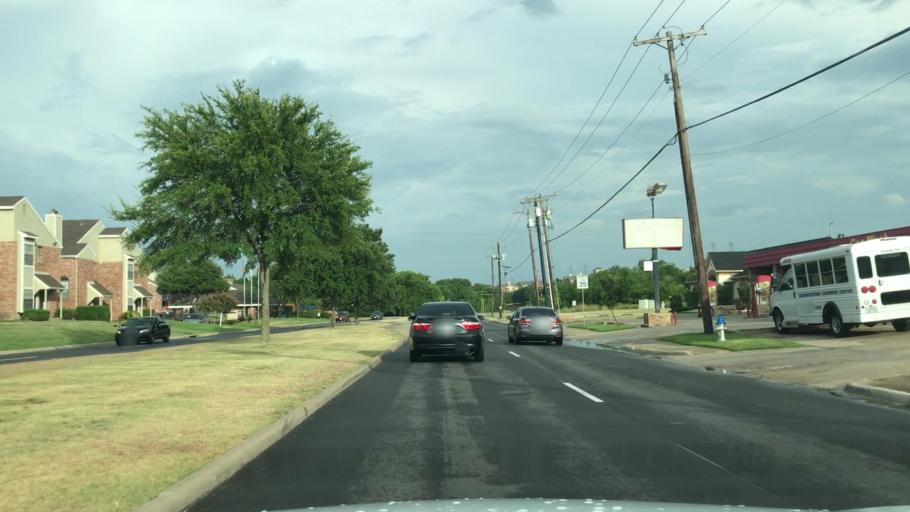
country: US
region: Texas
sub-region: Dallas County
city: Garland
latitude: 32.8411
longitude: -96.6241
